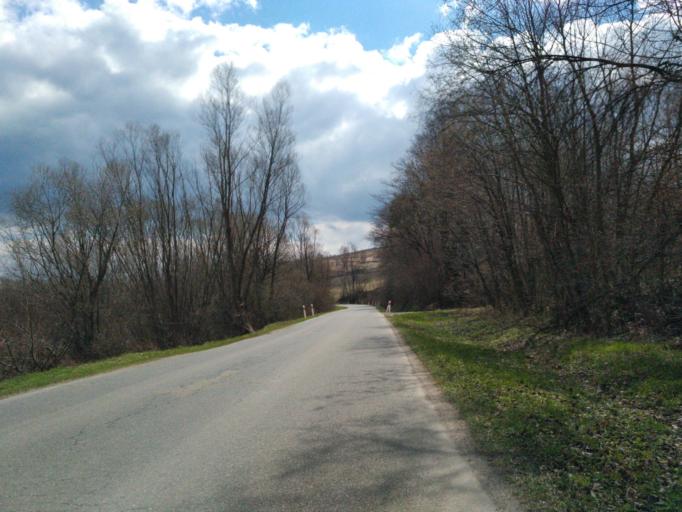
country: PL
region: Subcarpathian Voivodeship
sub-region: Powiat sanocki
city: Tyrawa Woloska
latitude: 49.5840
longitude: 22.3458
